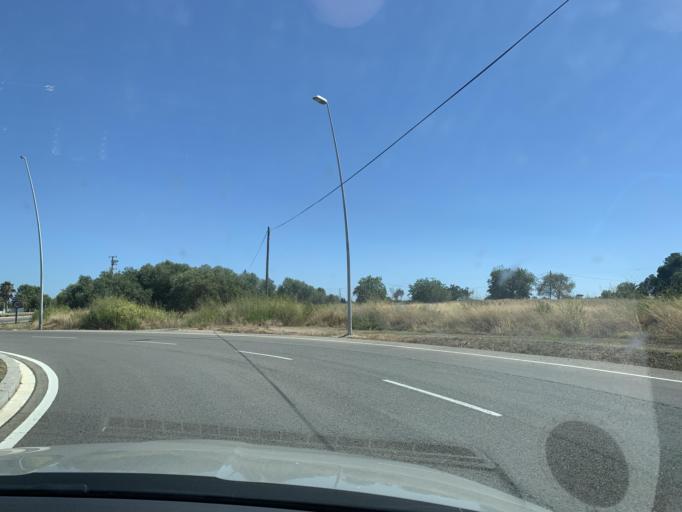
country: ES
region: Catalonia
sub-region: Provincia de Tarragona
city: Reus
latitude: 41.1429
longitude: 1.1274
